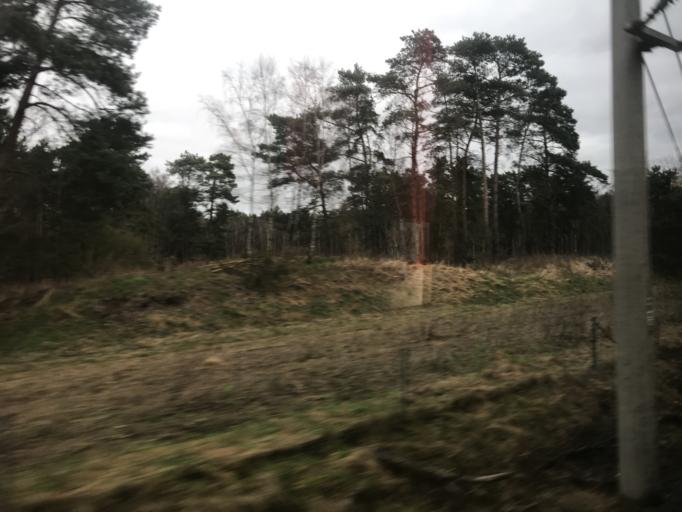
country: DE
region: Lower Saxony
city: Leiferde
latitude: 52.4565
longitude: 10.4396
